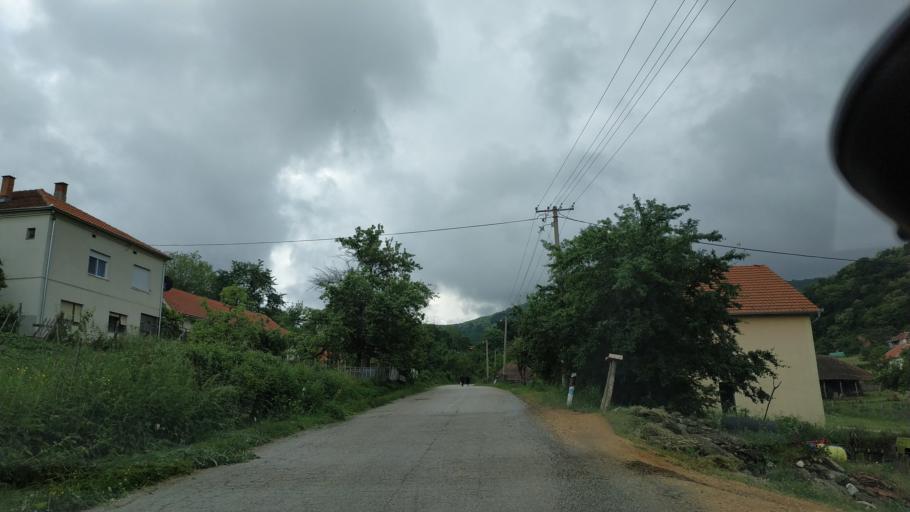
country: RS
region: Central Serbia
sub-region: Toplicki Okrug
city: Prokuplje
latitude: 43.3953
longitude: 21.5543
